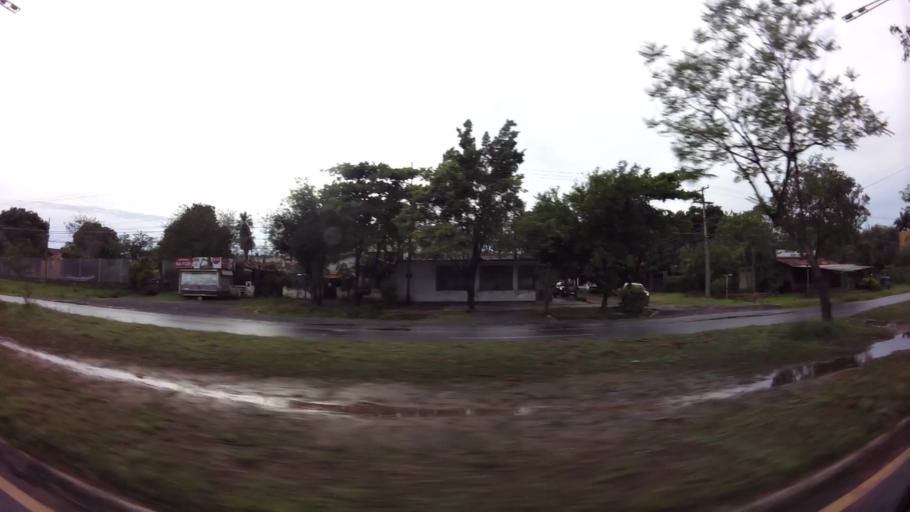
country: PY
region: Central
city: Fernando de la Mora
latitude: -25.2562
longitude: -57.5142
